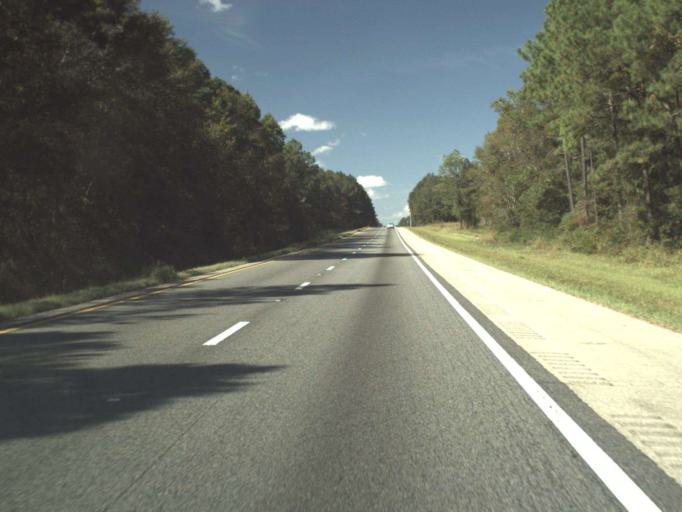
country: US
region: Florida
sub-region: Washington County
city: Chipley
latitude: 30.7456
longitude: -85.4703
